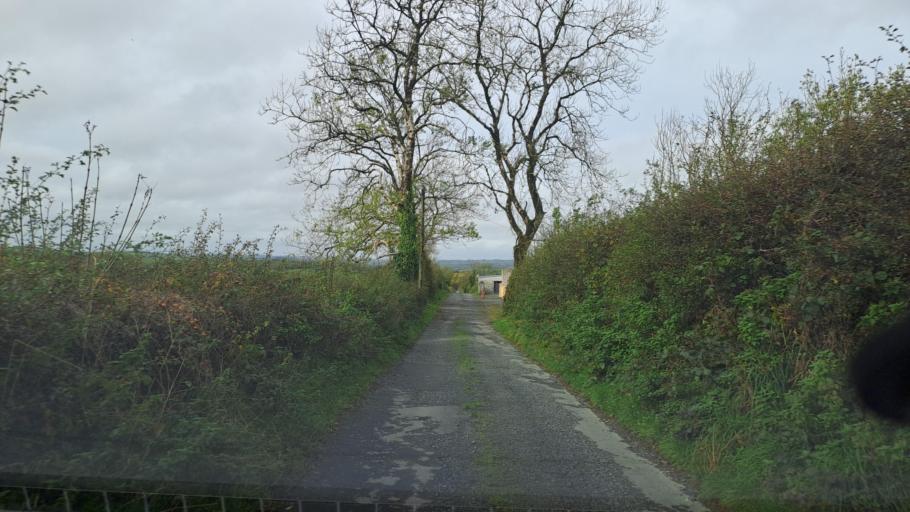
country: IE
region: Ulster
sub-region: County Monaghan
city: Carrickmacross
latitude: 54.0178
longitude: -6.8158
